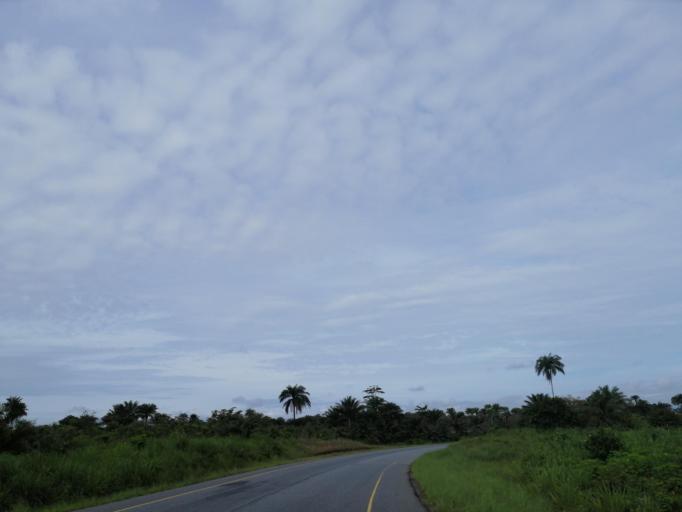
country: SL
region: Northern Province
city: Port Loko
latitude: 8.7674
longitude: -12.8855
